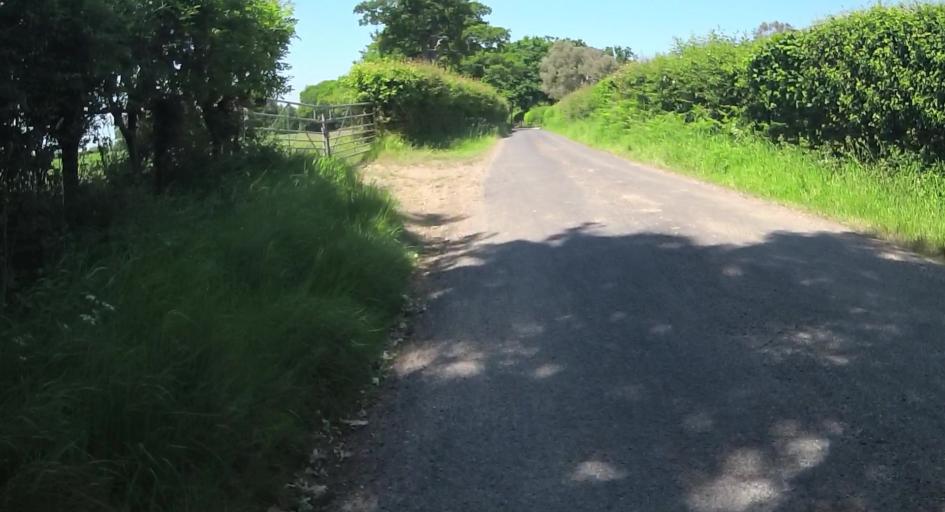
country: GB
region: England
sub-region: Hampshire
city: Tadley
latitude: 51.3333
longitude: -1.1848
